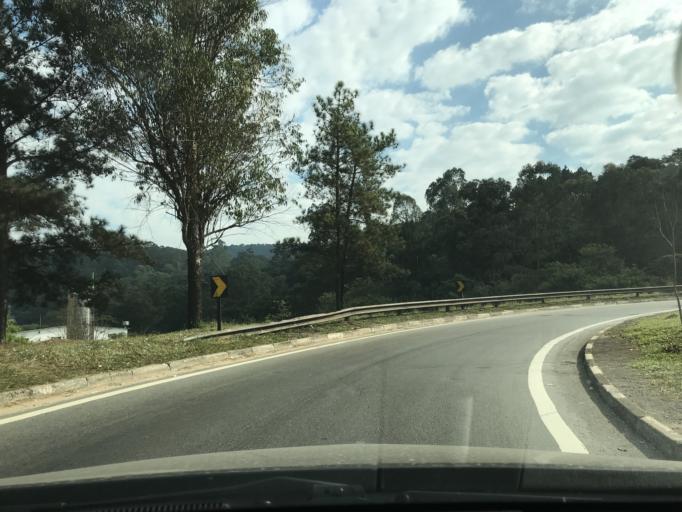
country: BR
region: Sao Paulo
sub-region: Cotia
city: Cotia
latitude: -23.6024
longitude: -46.9247
